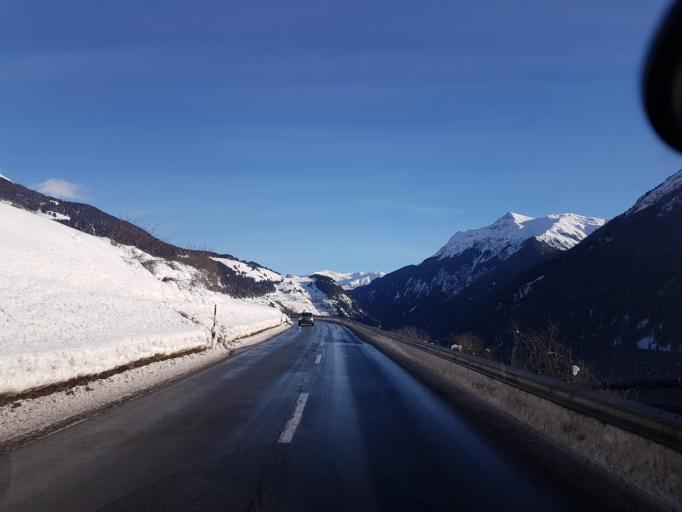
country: CH
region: Grisons
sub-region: Inn District
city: Scuol
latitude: 46.8163
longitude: 10.3562
